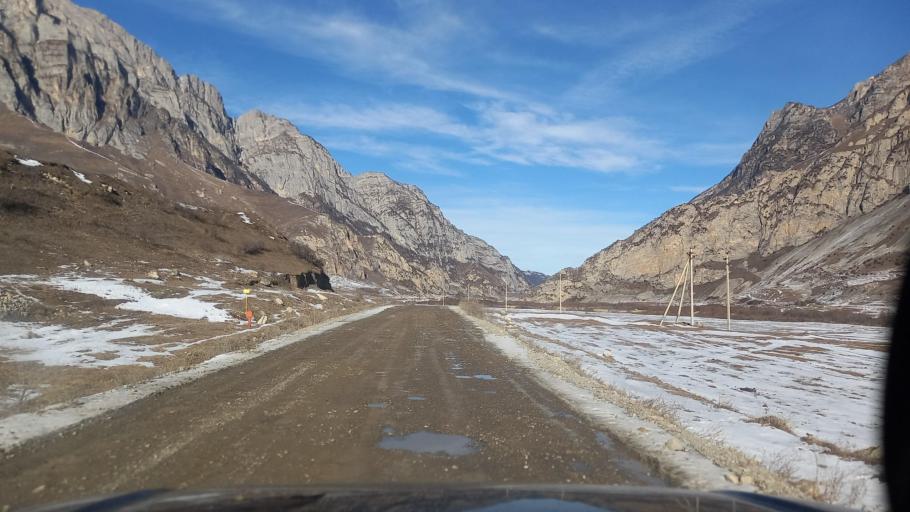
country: RU
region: North Ossetia
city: Verkhniy Fiagdon
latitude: 42.8515
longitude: 44.4444
